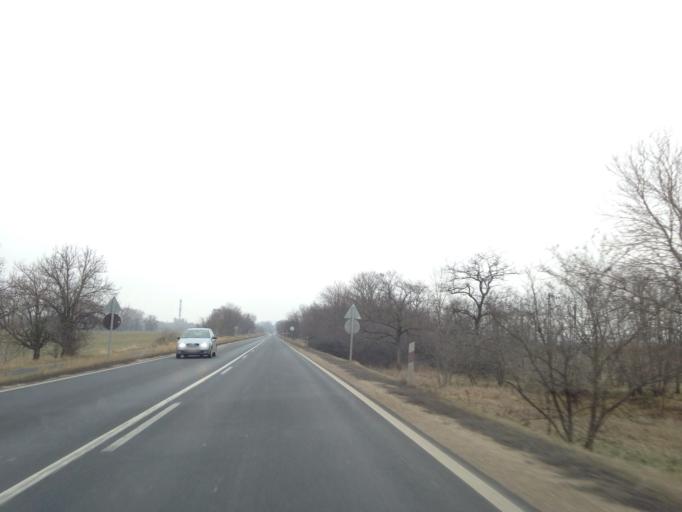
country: HU
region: Komarom-Esztergom
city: Almasfuzito
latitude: 47.7300
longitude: 18.2291
